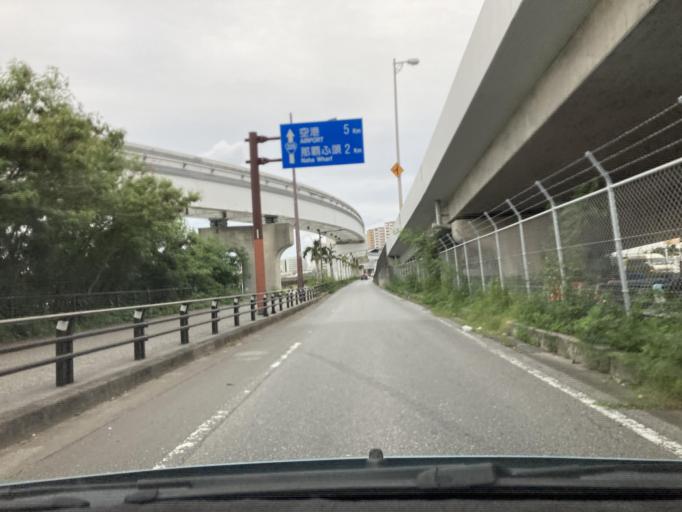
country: JP
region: Okinawa
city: Naha-shi
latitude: 26.2025
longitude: 127.6798
